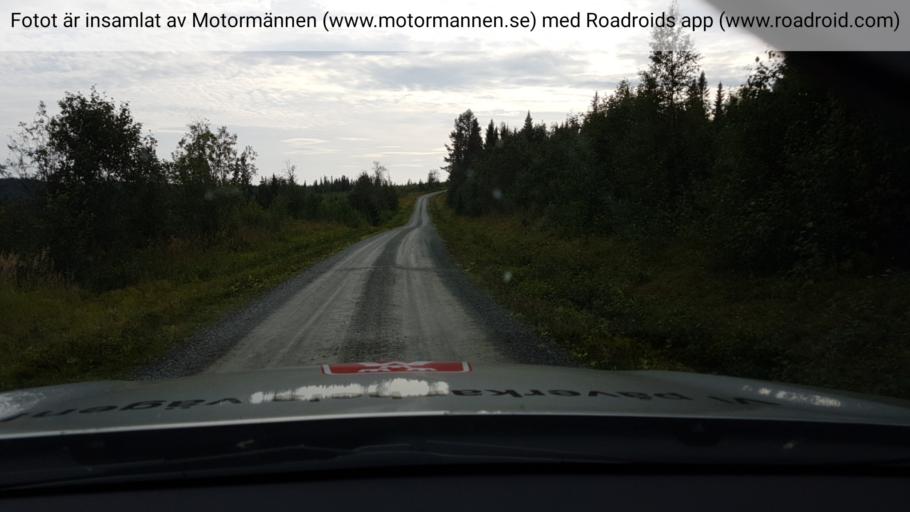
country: SE
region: Jaemtland
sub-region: Krokoms Kommun
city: Valla
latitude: 63.5790
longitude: 13.9437
